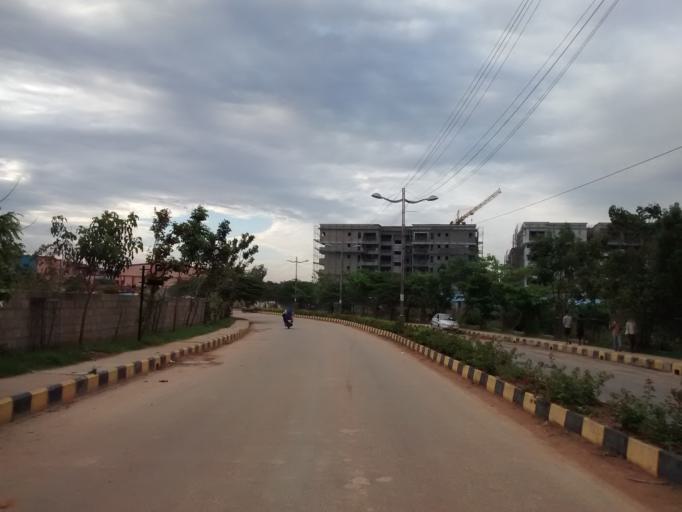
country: IN
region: Karnataka
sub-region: Bangalore Urban
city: Bangalore
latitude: 12.9518
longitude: 77.6896
